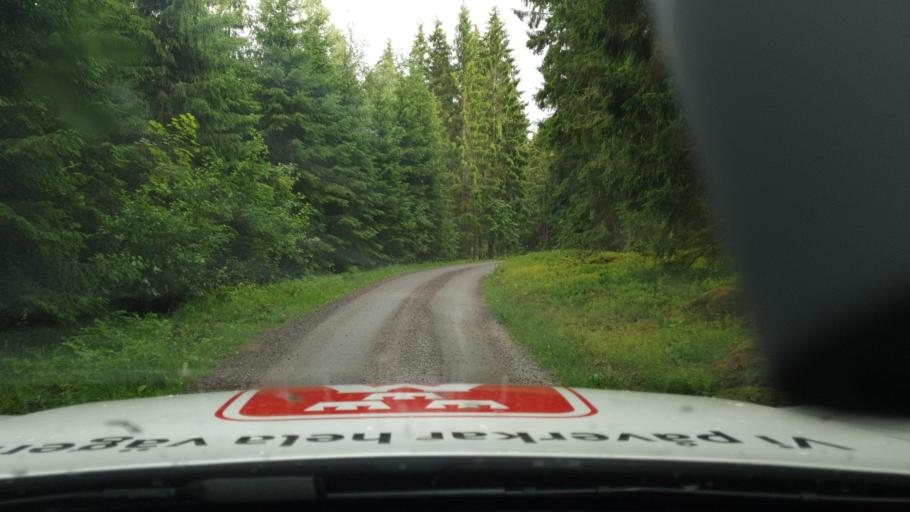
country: SE
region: Vaestra Goetaland
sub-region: Falkopings Kommun
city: Falkoeping
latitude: 58.0525
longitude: 13.6631
